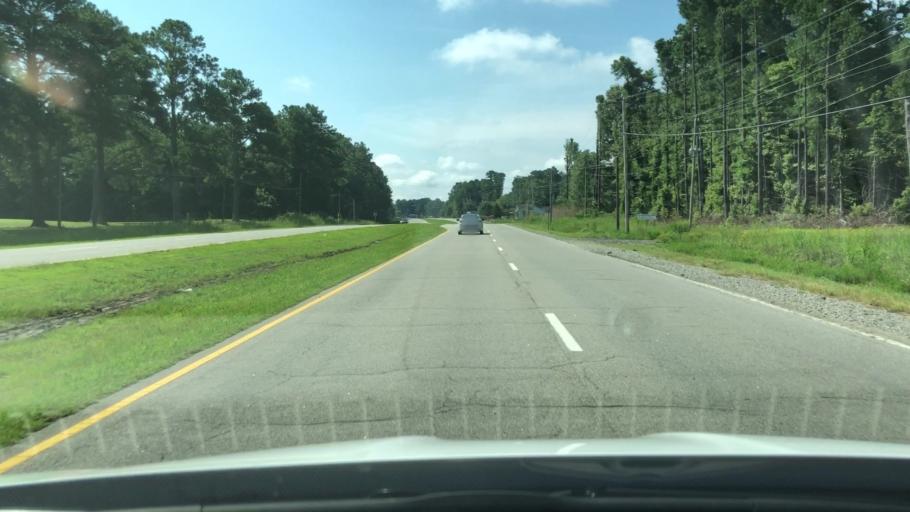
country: US
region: North Carolina
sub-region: Bertie County
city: Windsor
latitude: 35.9718
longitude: -76.9552
